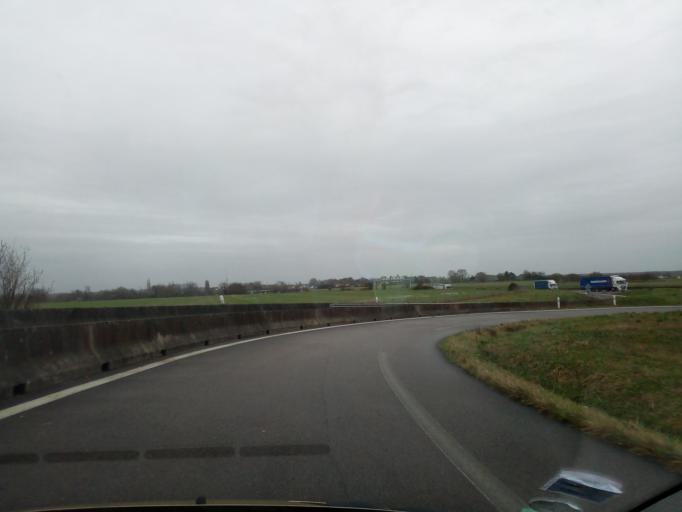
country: FR
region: Haute-Normandie
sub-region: Departement de l'Eure
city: Bourg-Achard
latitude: 49.3652
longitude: 0.8323
